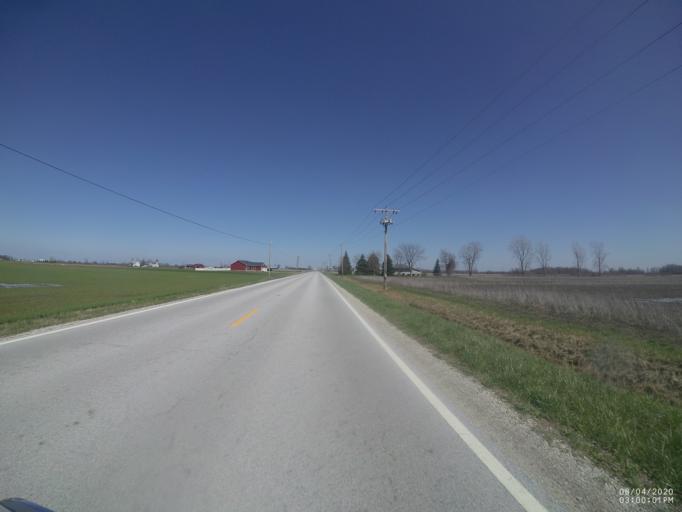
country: US
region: Ohio
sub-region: Sandusky County
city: Stony Prairie
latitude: 41.3225
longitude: -83.2438
